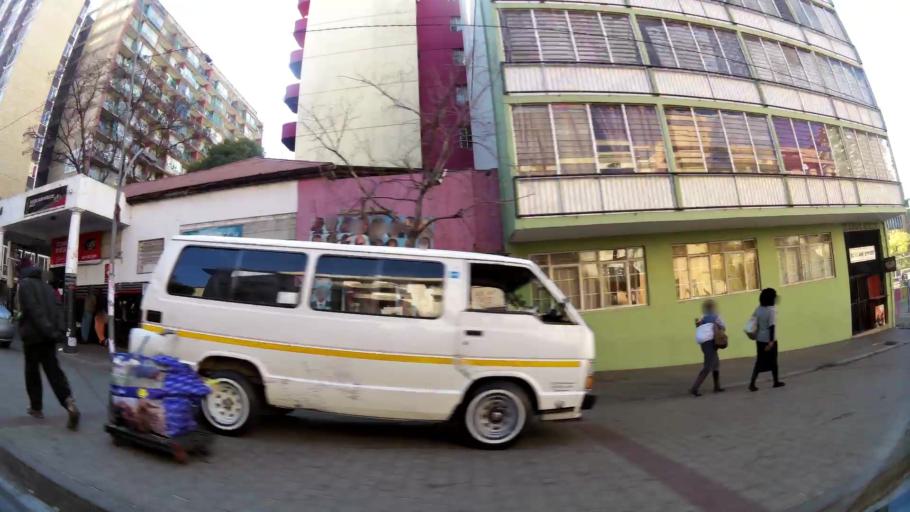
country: ZA
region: Gauteng
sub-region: City of Johannesburg Metropolitan Municipality
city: Johannesburg
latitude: -26.1915
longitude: 28.0495
